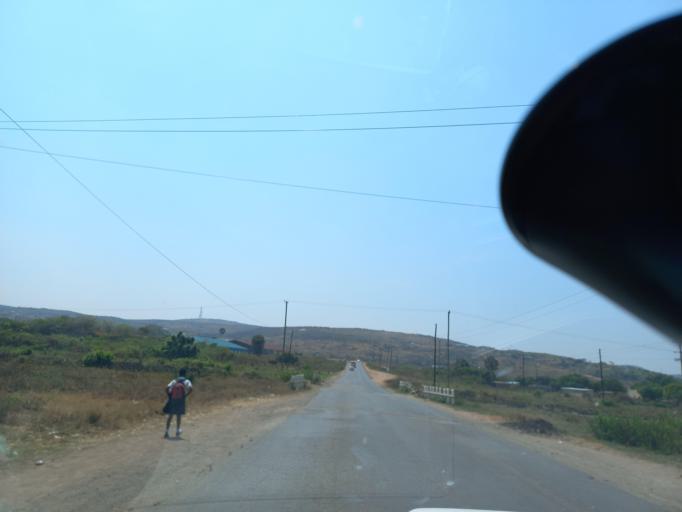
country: ZM
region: Lusaka
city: Kafue
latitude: -15.7588
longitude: 28.1753
